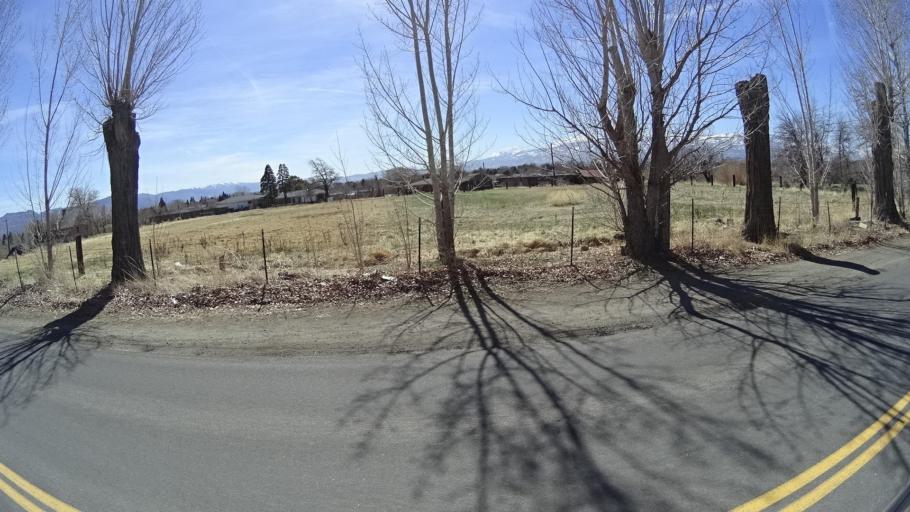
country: US
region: Nevada
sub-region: Washoe County
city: Sparks
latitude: 39.5539
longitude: -119.7765
